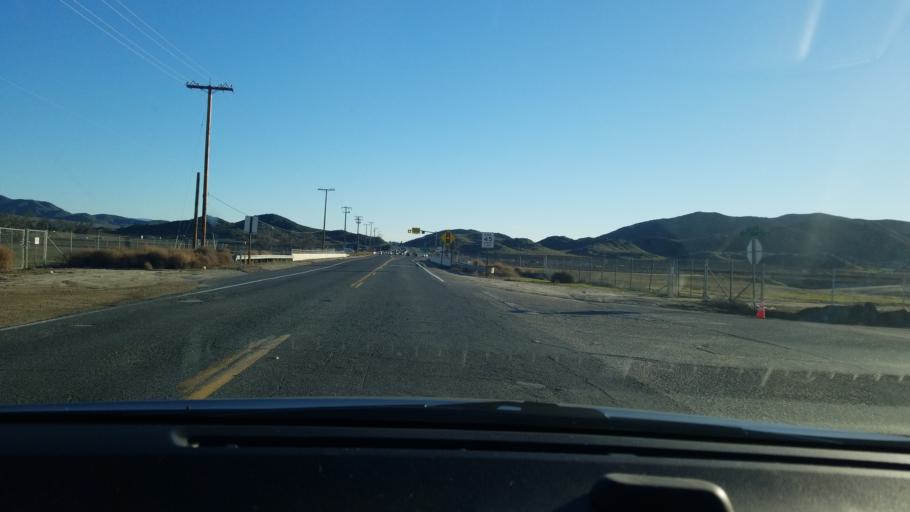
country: US
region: California
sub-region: Riverside County
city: Winchester
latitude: 33.7000
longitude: -117.0849
